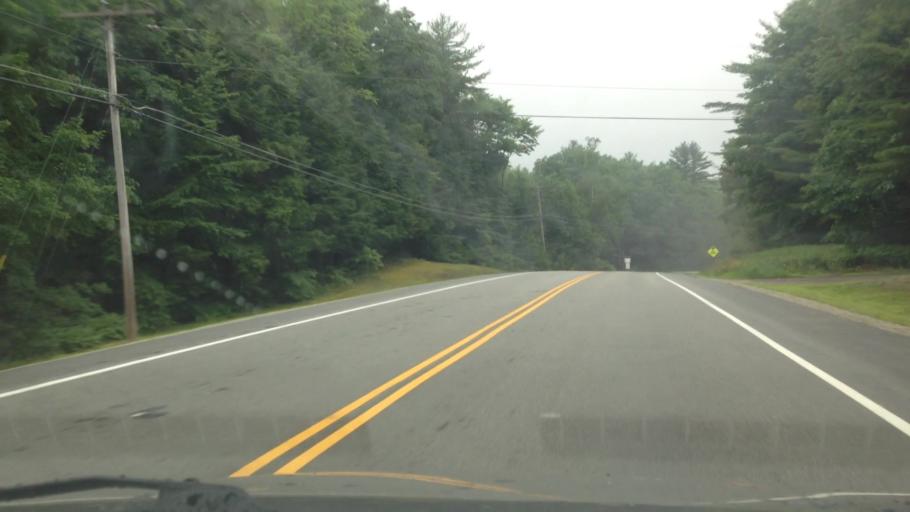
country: US
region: New Hampshire
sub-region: Cheshire County
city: Marlborough
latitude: 42.8798
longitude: -72.1911
